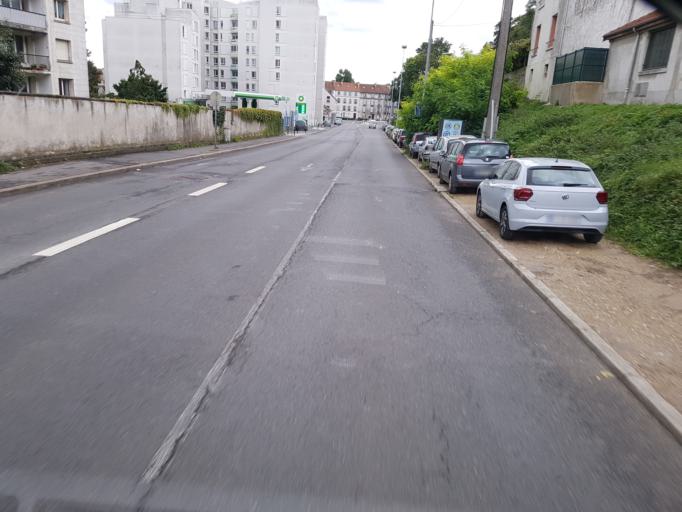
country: FR
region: Ile-de-France
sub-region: Departement de Seine-et-Marne
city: Meaux
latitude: 48.9610
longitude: 2.8712
